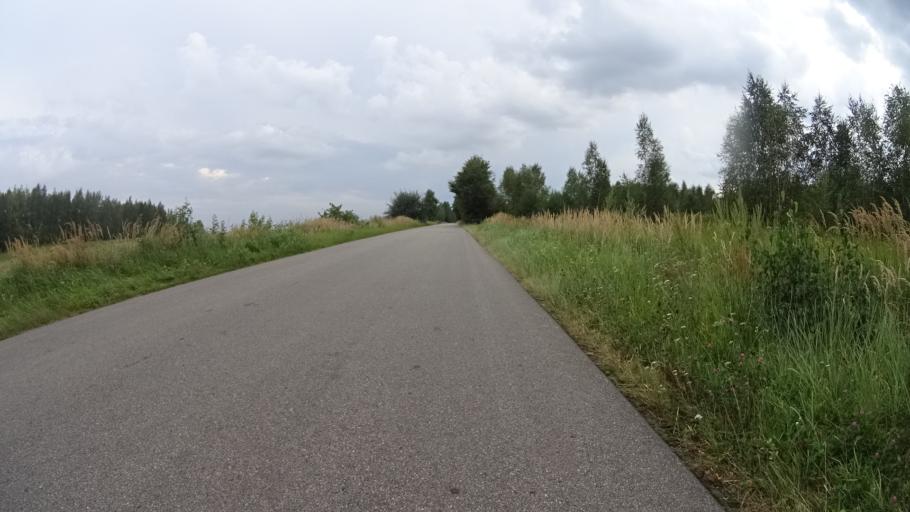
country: PL
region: Masovian Voivodeship
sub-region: Powiat grojecki
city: Goszczyn
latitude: 51.6822
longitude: 20.8607
